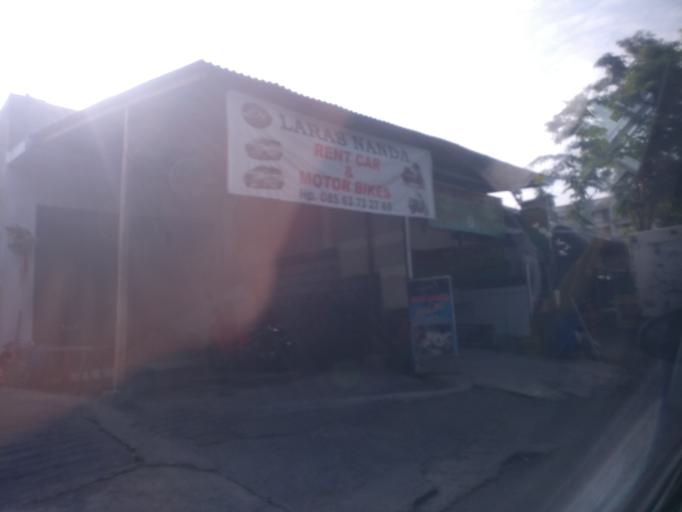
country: ID
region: Bali
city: Kuta
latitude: -8.6806
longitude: 115.1629
